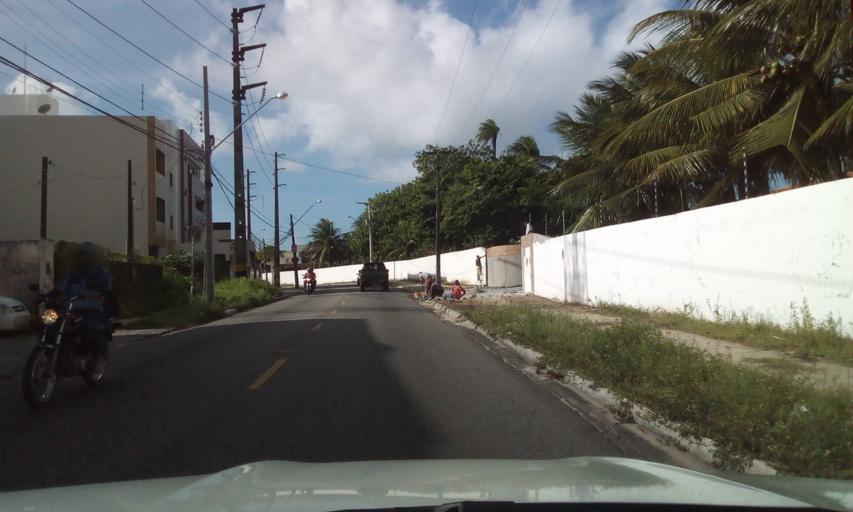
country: BR
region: Paraiba
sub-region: Joao Pessoa
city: Joao Pessoa
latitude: -7.1746
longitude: -34.8629
